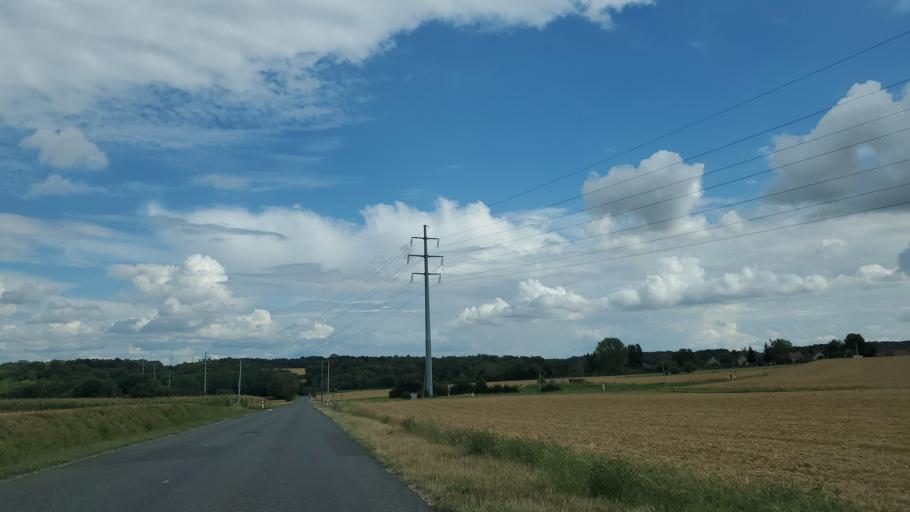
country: FR
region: Ile-de-France
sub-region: Departement de Seine-et-Marne
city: Chailly-en-Brie
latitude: 48.7818
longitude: 3.1603
